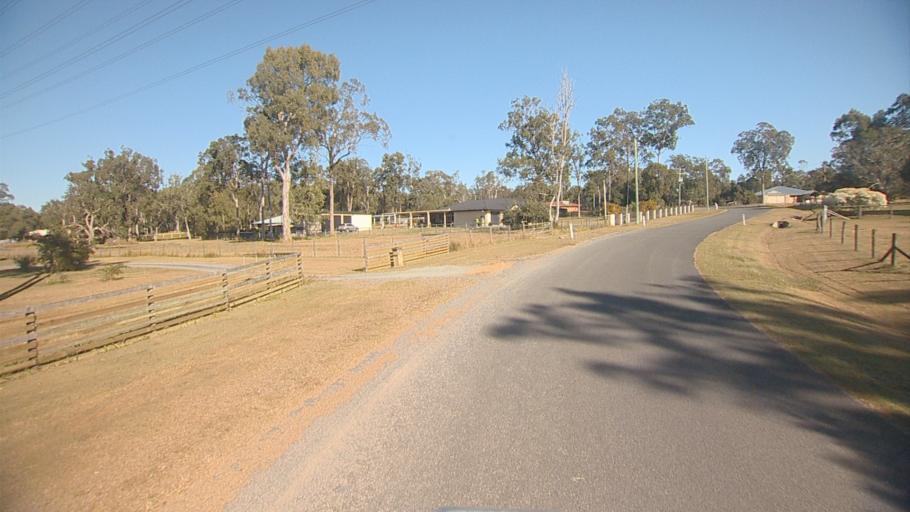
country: AU
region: Queensland
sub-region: Logan
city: Chambers Flat
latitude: -27.7740
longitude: 153.0803
